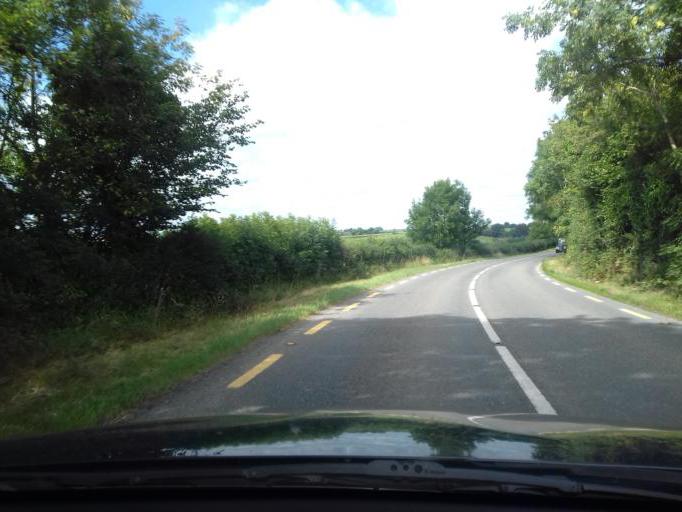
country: IE
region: Leinster
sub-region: Wicklow
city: Baltinglass
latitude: 52.9898
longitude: -6.6556
